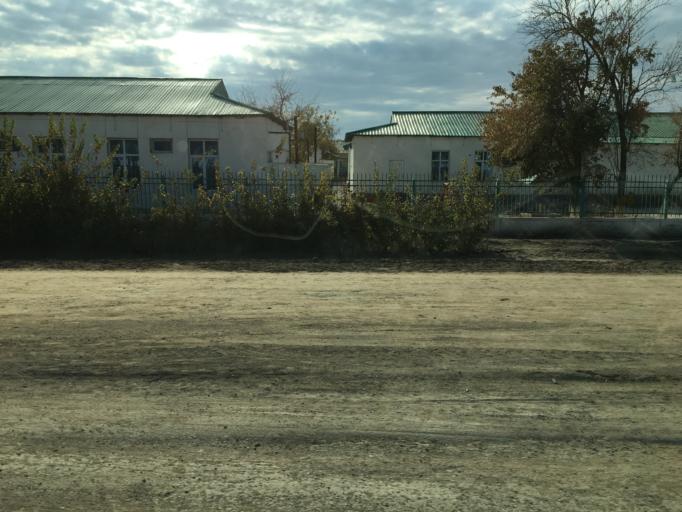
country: TM
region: Ahal
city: Tejen
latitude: 37.3708
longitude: 60.5045
